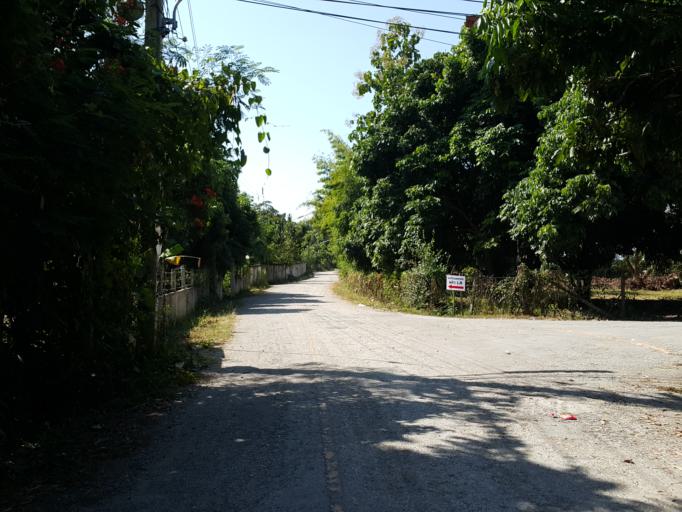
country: TH
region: Chiang Mai
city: San Sai
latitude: 18.8757
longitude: 99.1623
